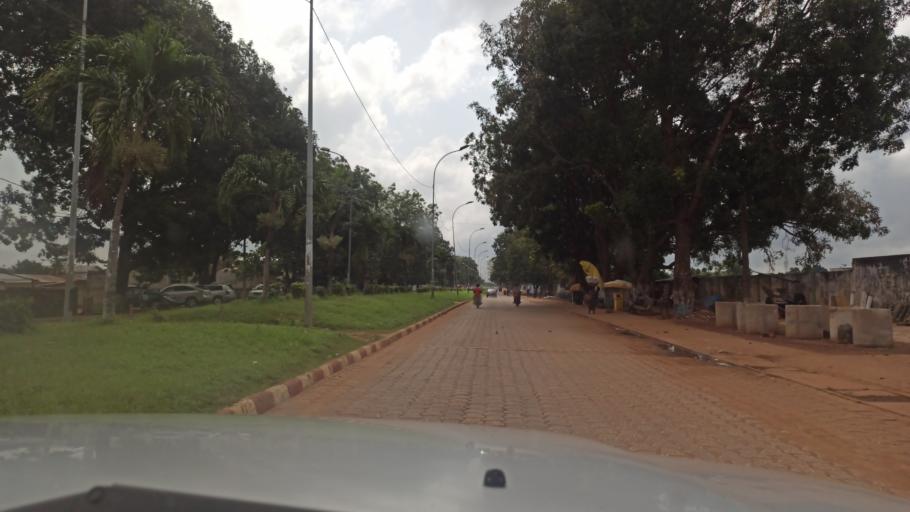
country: BJ
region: Queme
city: Porto-Novo
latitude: 6.4790
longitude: 2.6342
